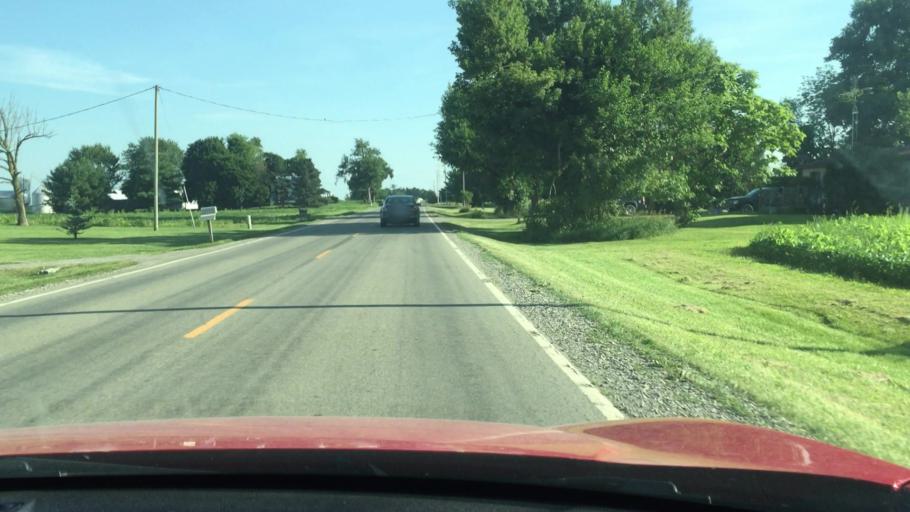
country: US
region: Ohio
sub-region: Hardin County
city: Ada
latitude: 40.6862
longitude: -83.8573
